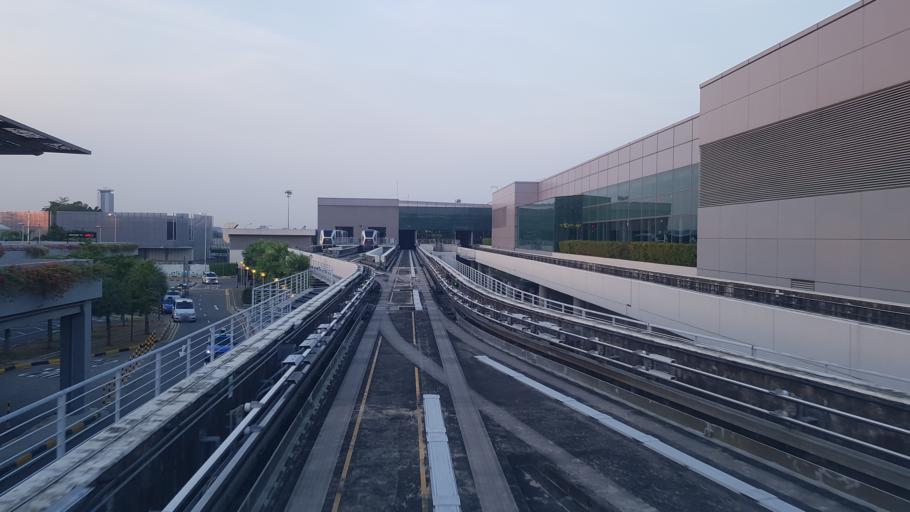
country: SG
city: Singapore
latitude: 1.3515
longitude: 103.9845
